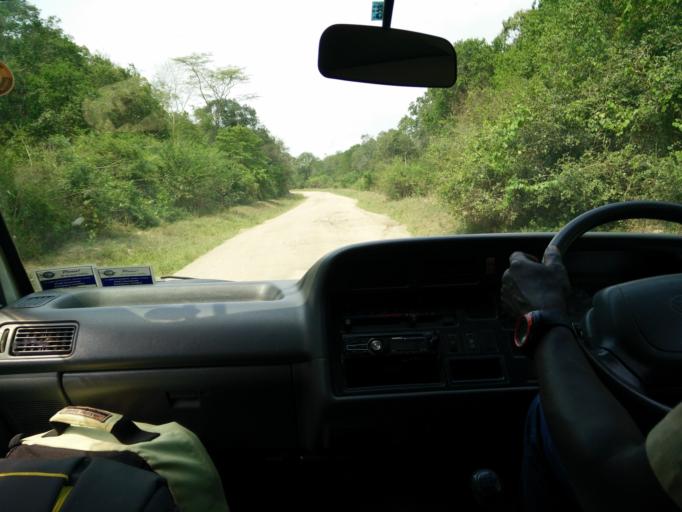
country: UG
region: Western Region
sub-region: Rubirizi District
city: Rubirizi
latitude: -0.3584
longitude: 29.8693
